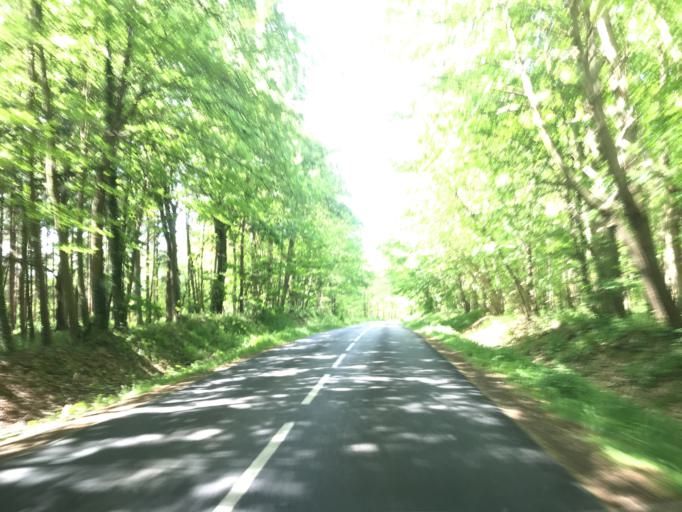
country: FR
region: Haute-Normandie
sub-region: Departement de l'Eure
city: Nassandres
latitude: 49.1539
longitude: 0.8131
